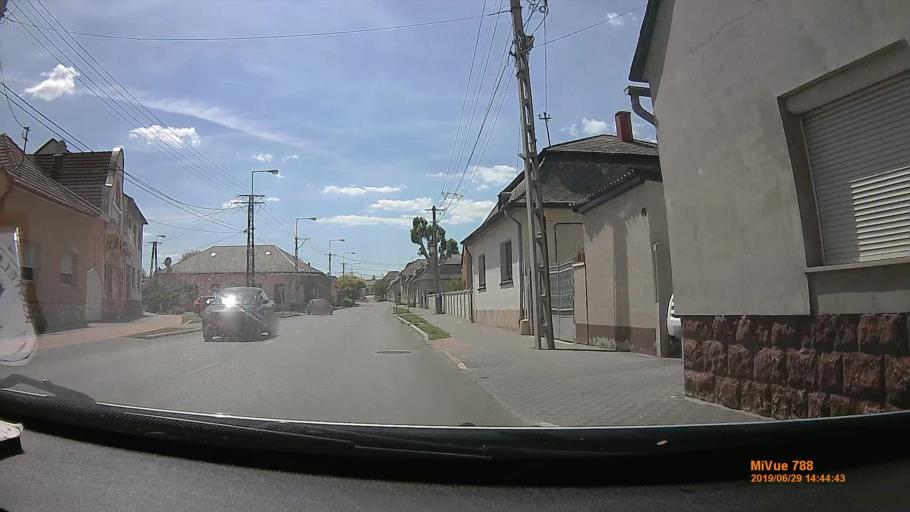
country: HU
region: Komarom-Esztergom
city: Nyergesujfalu
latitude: 47.7618
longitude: 18.5456
